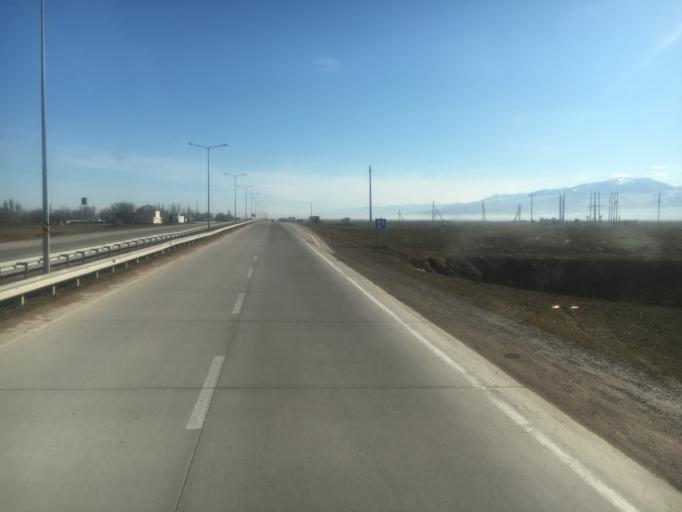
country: KZ
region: Zhambyl
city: Merke
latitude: 42.8895
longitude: 72.9821
